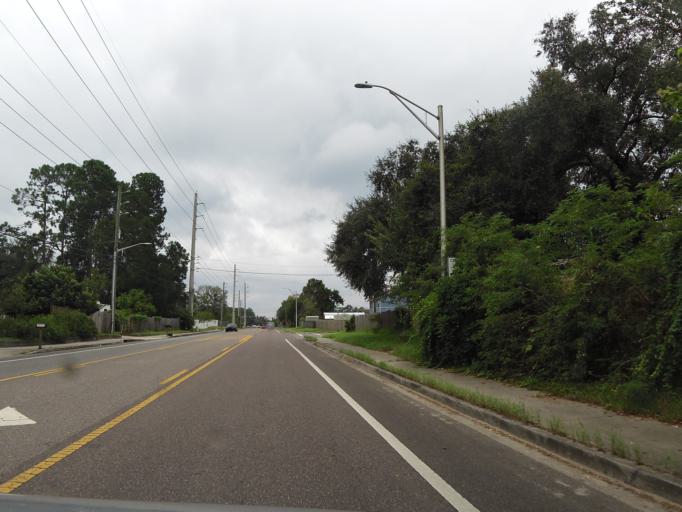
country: US
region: Florida
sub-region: Clay County
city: Bellair-Meadowbrook Terrace
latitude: 30.2067
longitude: -81.7648
